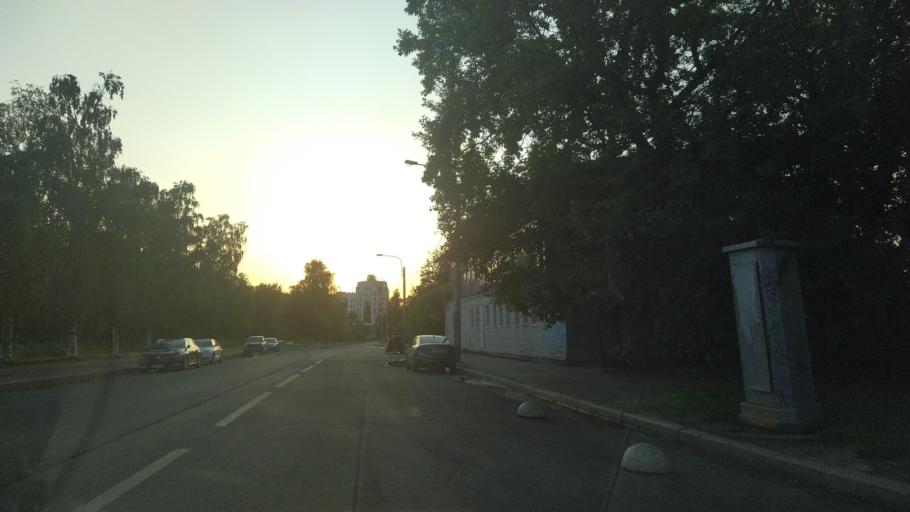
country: RU
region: Leningrad
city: Krestovskiy ostrov
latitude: 59.9557
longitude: 30.2804
